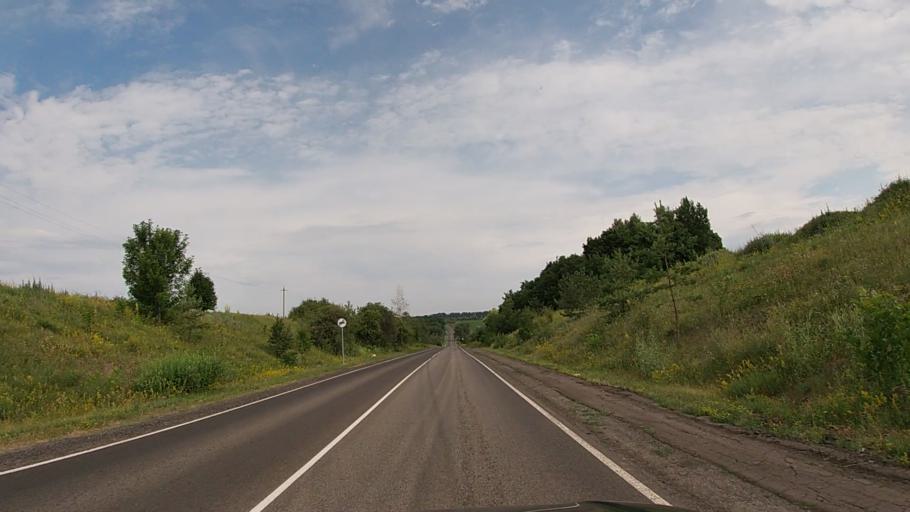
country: RU
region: Belgorod
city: Krasnaya Yaruga
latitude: 50.8236
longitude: 35.5002
